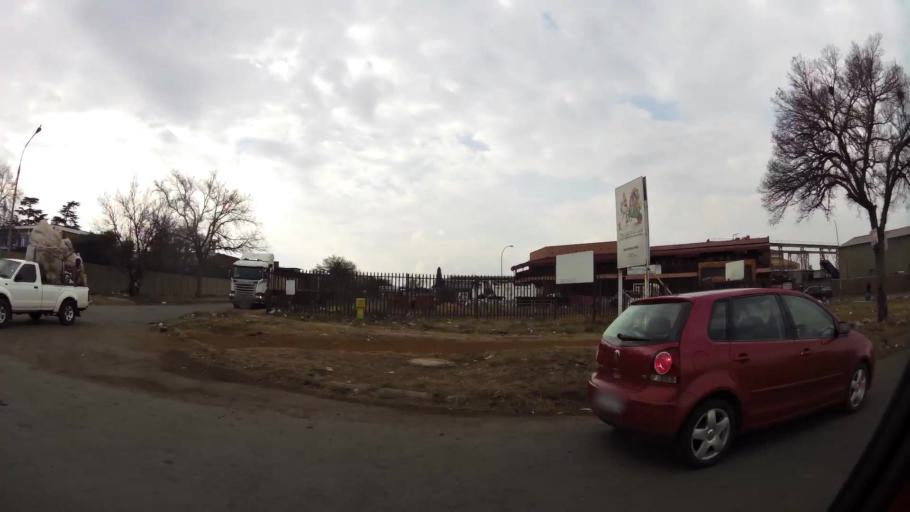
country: ZA
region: Gauteng
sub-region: Sedibeng District Municipality
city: Vanderbijlpark
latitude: -26.6620
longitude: 27.8512
